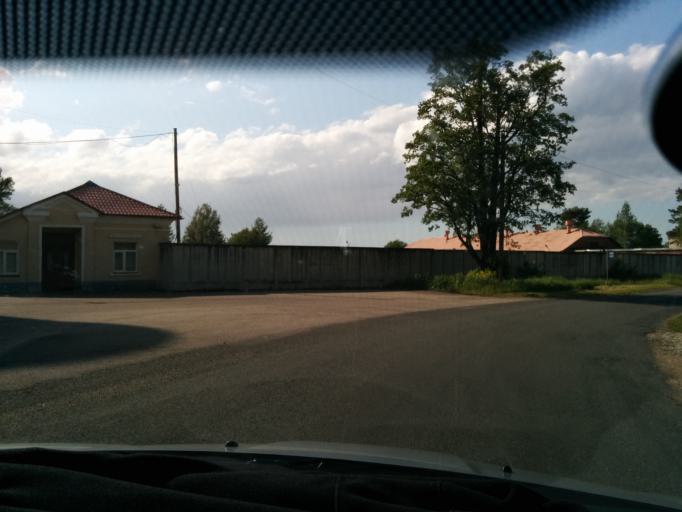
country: EE
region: Harju
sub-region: Loksa linn
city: Loksa
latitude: 59.5868
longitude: 25.7075
